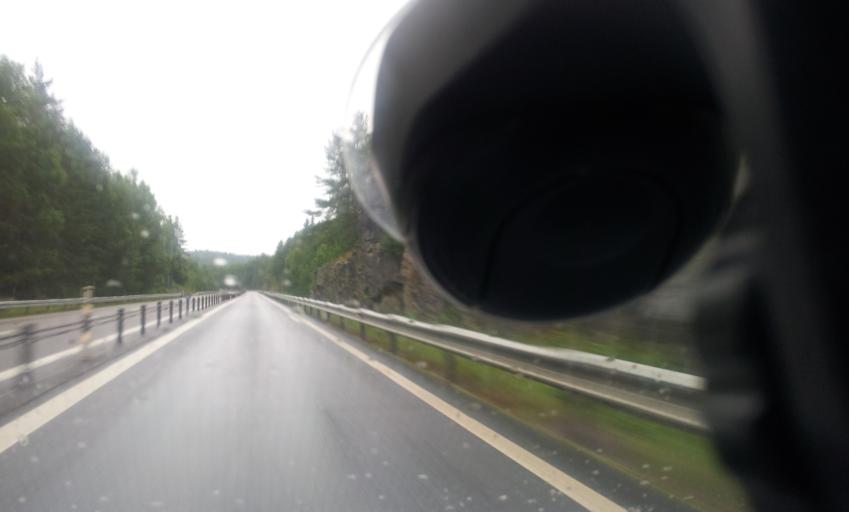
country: SE
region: OEstergoetland
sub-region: Valdemarsviks Kommun
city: Valdemarsvik
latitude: 58.1036
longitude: 16.5399
